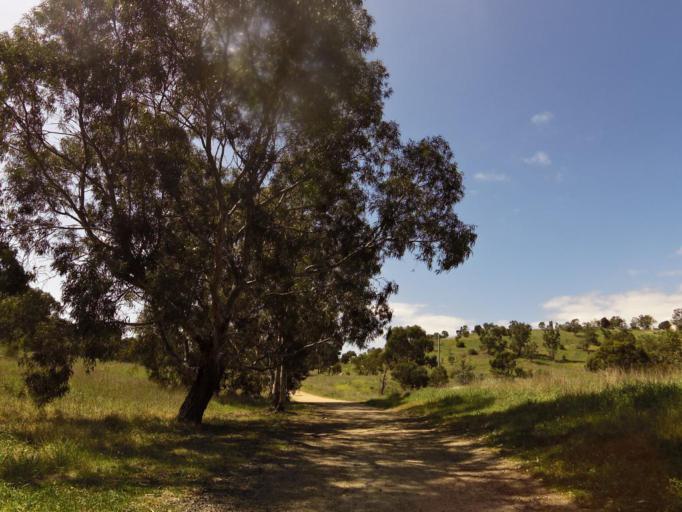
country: AU
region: Victoria
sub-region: Moonee Valley
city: Essendon West
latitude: -37.7558
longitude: 144.8779
